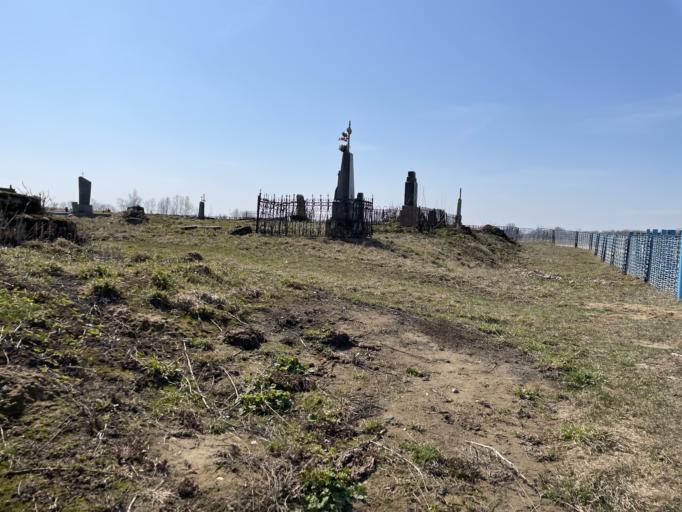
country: BY
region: Minsk
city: Snow
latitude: 53.1468
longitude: 26.3589
